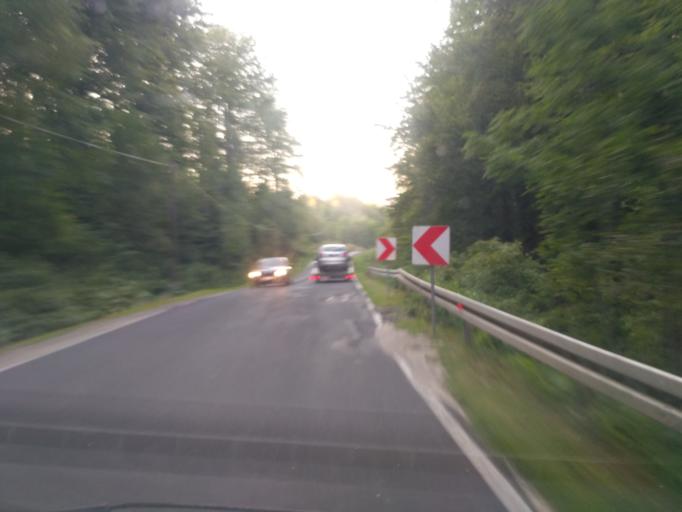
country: PL
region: Subcarpathian Voivodeship
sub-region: Powiat krosnienski
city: Korczyna
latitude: 49.7574
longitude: 21.7939
